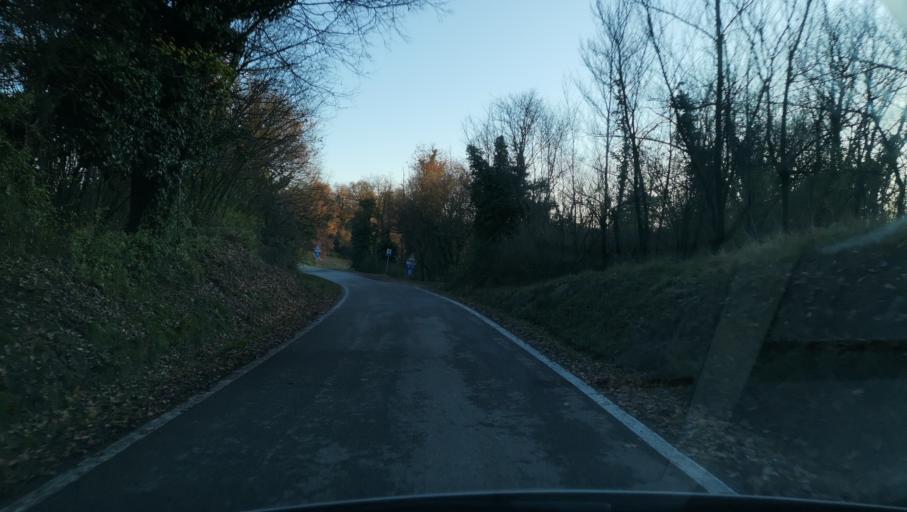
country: IT
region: Piedmont
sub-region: Provincia di Torino
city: Cinzano
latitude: 45.0831
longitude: 7.9247
